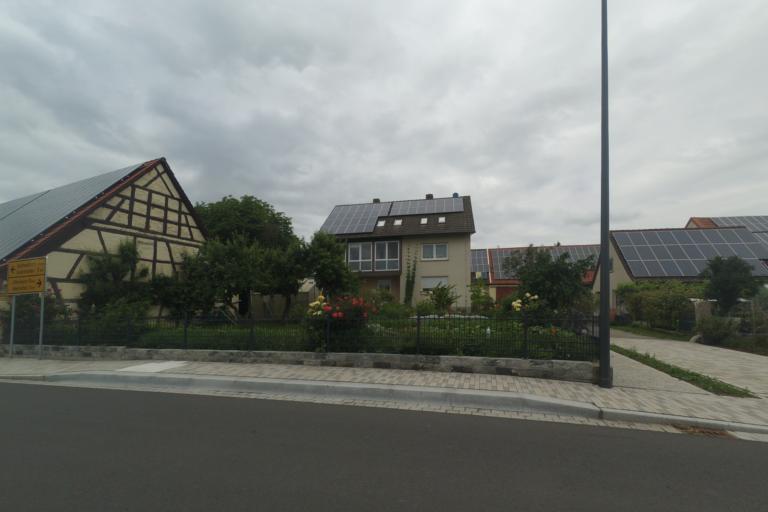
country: DE
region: Bavaria
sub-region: Regierungsbezirk Mittelfranken
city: Simmershofen
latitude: 49.5309
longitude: 10.1217
